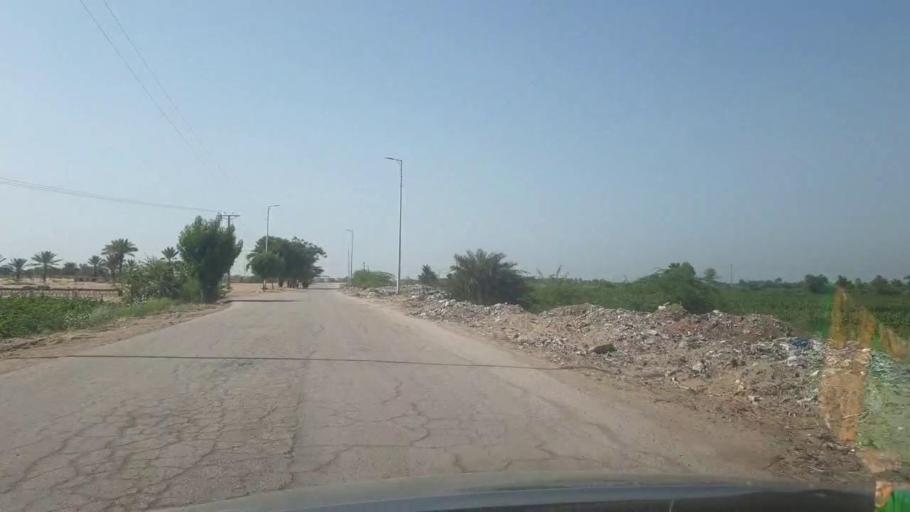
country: PK
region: Sindh
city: Rohri
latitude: 27.5074
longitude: 69.0367
